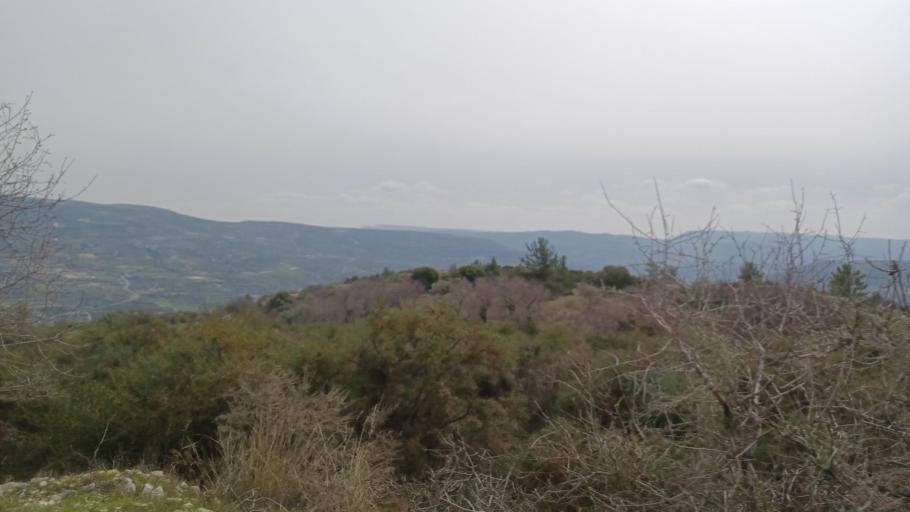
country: CY
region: Limassol
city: Pachna
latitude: 34.8595
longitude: 32.7081
